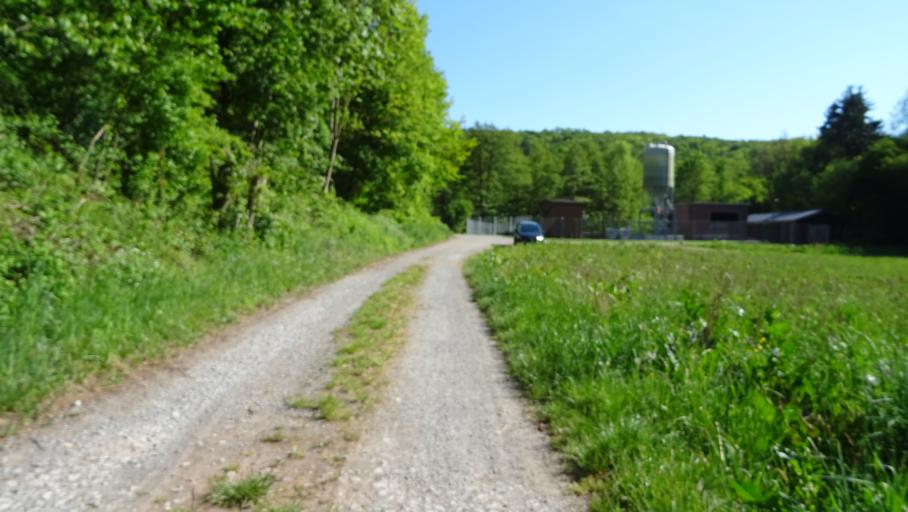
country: DE
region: Baden-Wuerttemberg
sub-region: Karlsruhe Region
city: Limbach
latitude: 49.4036
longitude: 9.2083
